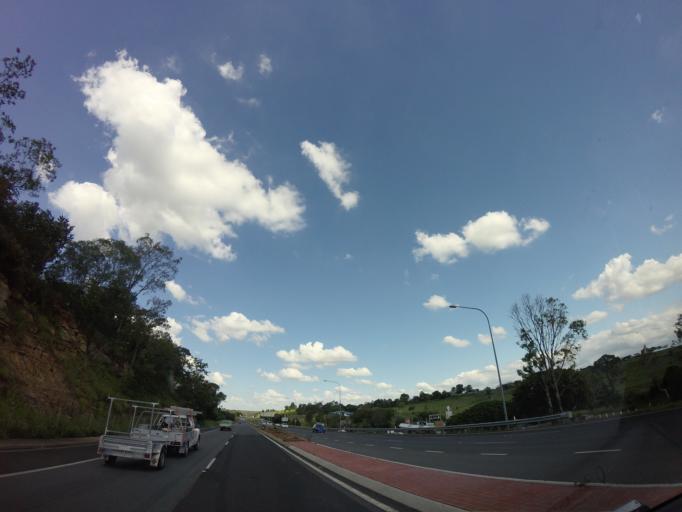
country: AU
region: Queensland
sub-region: Ipswich
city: Thagoona
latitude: -27.5631
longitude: 152.5819
